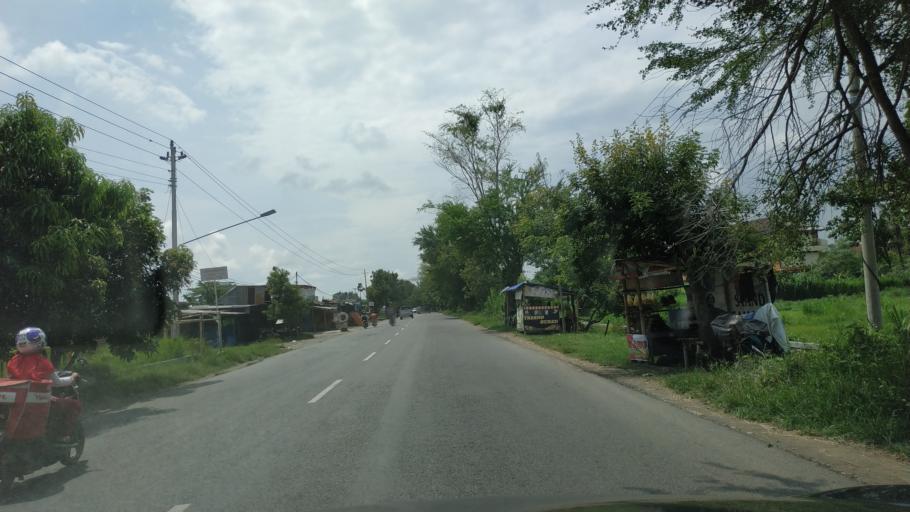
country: ID
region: Central Java
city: Adiwerna
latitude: -6.9396
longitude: 109.1247
